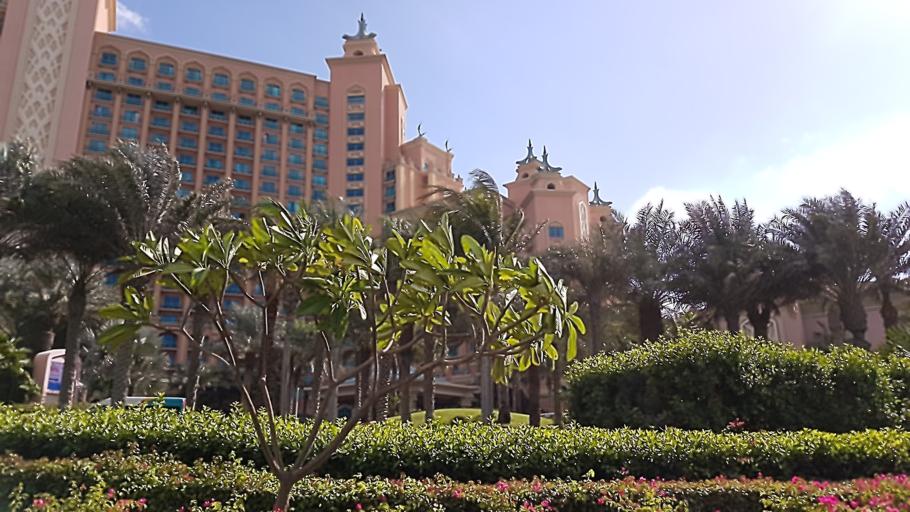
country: AE
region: Dubai
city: Dubai
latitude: 25.1308
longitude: 55.1157
